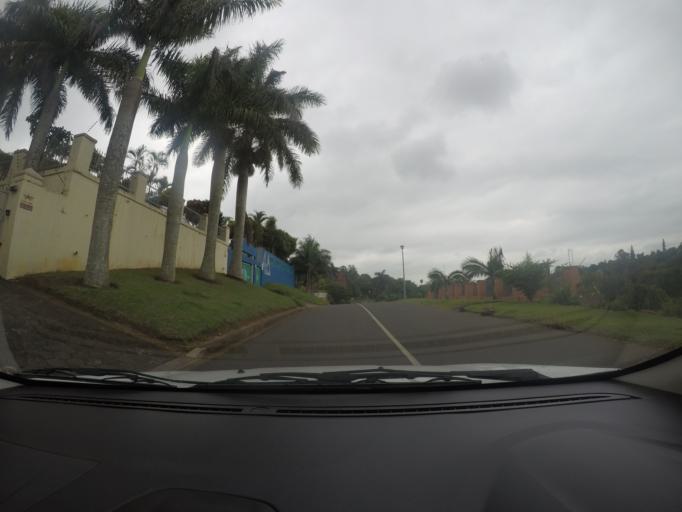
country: ZA
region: KwaZulu-Natal
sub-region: uThungulu District Municipality
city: Empangeni
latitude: -28.7621
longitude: 31.8876
